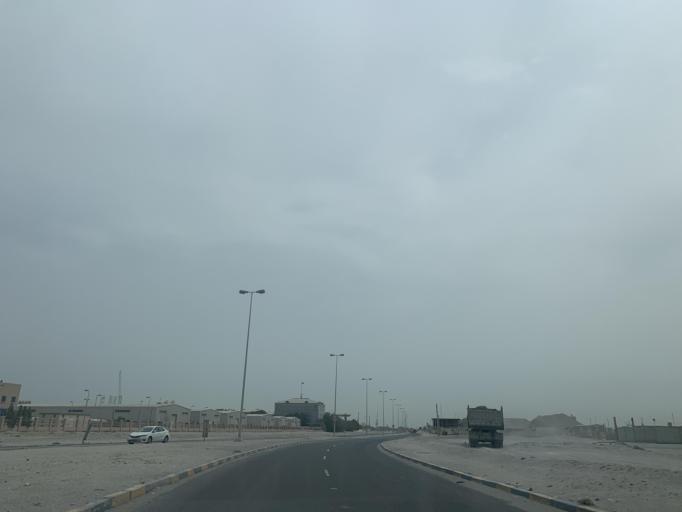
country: BH
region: Muharraq
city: Al Hadd
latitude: 26.2106
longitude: 50.6584
